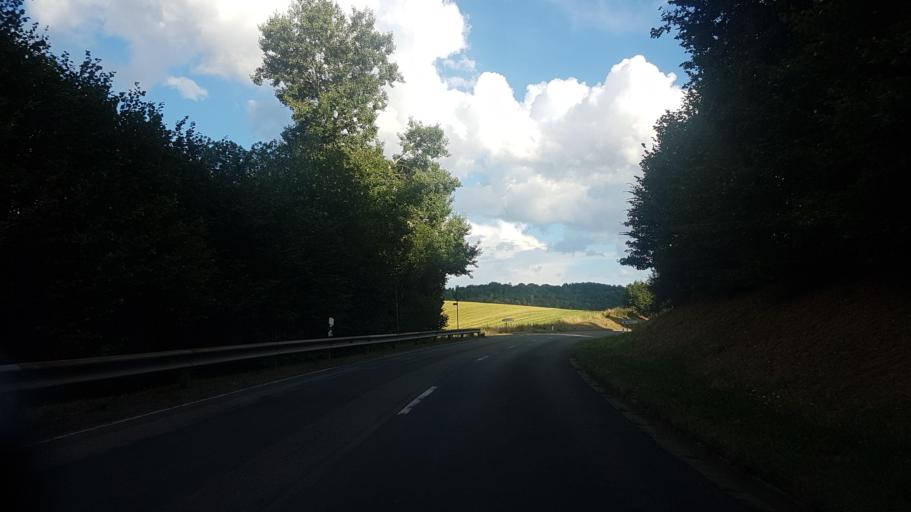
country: DE
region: Rheinland-Pfalz
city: Dienstweiler
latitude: 49.6360
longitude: 7.1927
